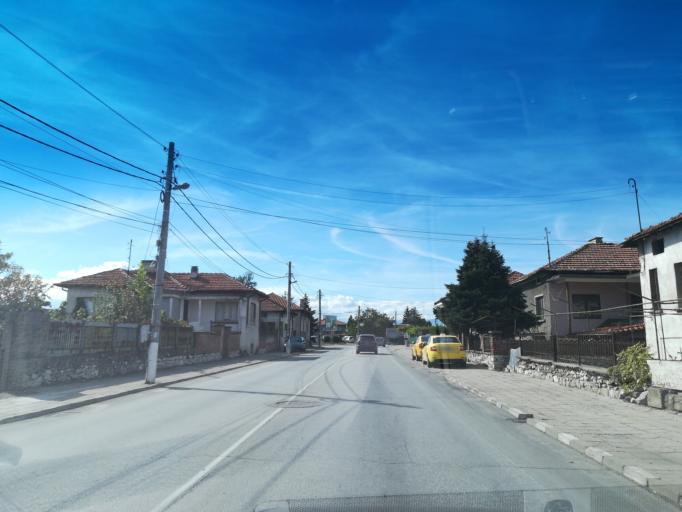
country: BG
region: Plovdiv
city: Stamboliyski
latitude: 42.1189
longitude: 24.5704
